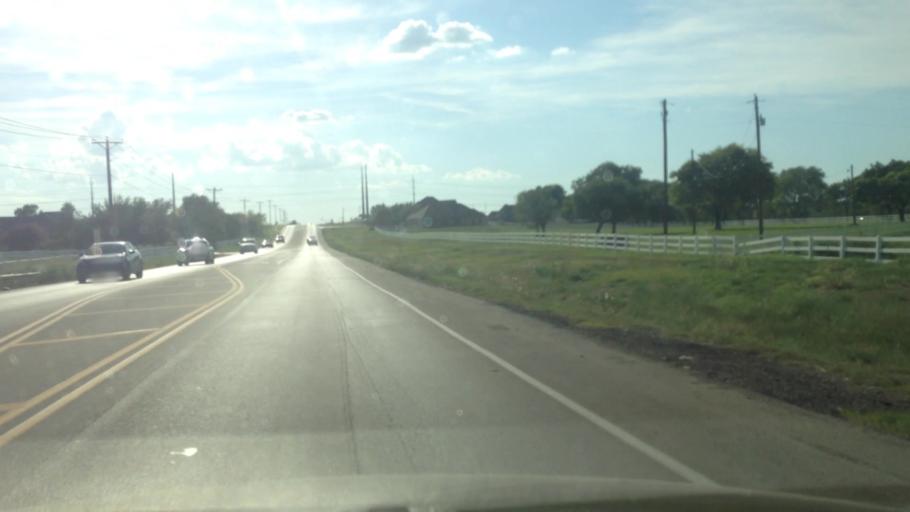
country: US
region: Texas
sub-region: Tarrant County
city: Haslet
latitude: 32.9244
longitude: -97.3855
